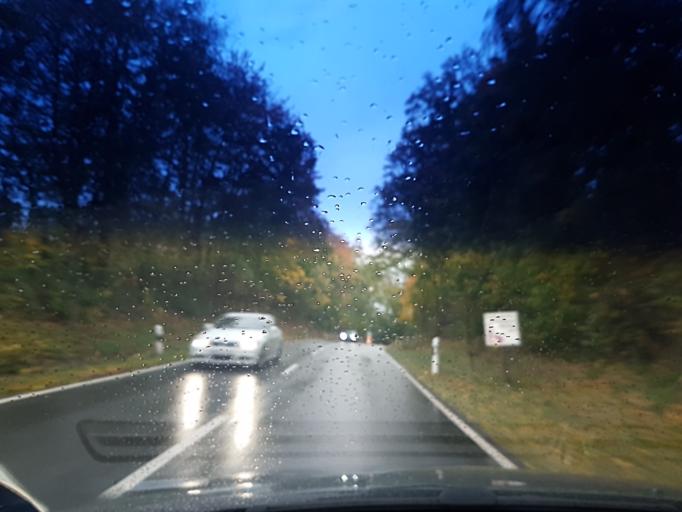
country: DE
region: Bavaria
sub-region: Upper Franconia
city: Pommersfelden
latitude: 49.7697
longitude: 10.8018
